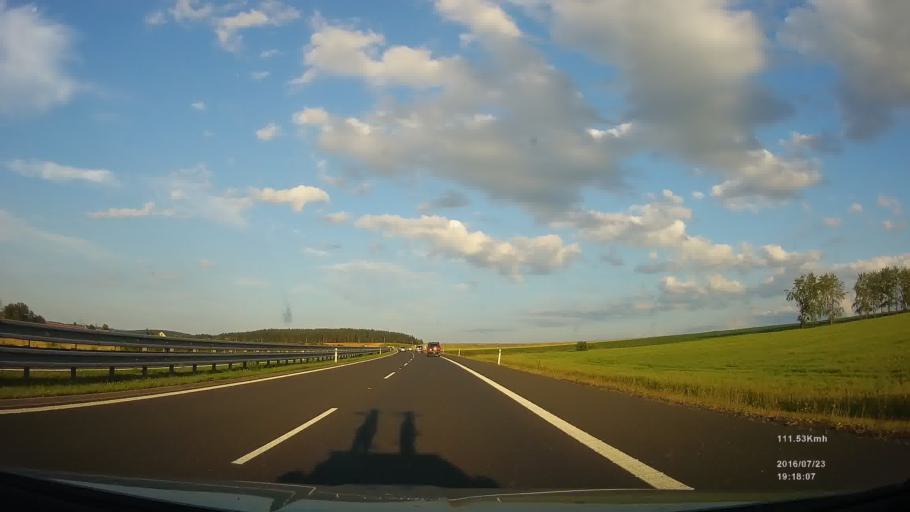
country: SK
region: Presovsky
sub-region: Okres Poprad
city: Poprad
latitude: 49.0480
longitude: 20.3743
